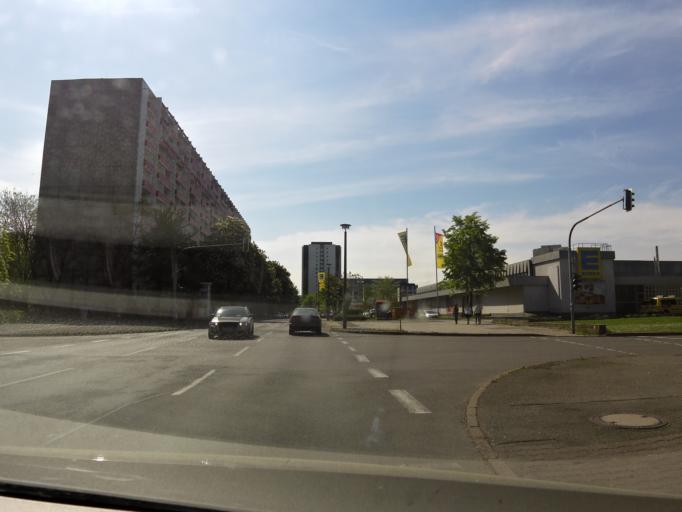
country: DE
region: Thuringia
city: Erfurt
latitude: 51.0107
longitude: 10.9987
